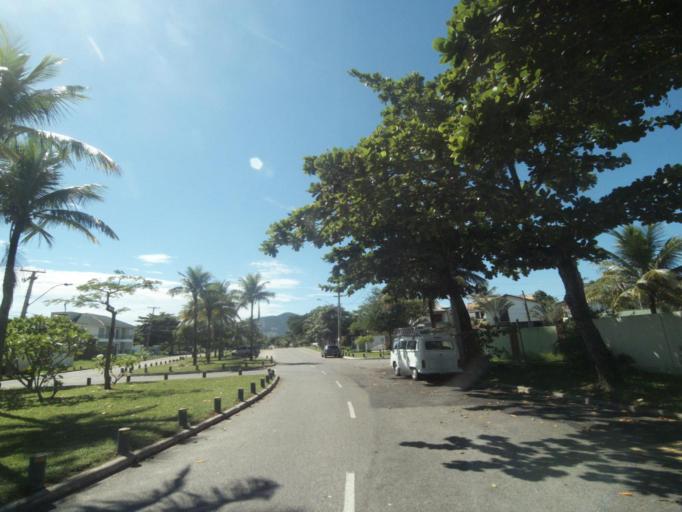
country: BR
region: Rio de Janeiro
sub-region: Niteroi
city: Niteroi
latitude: -22.9575
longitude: -43.0642
